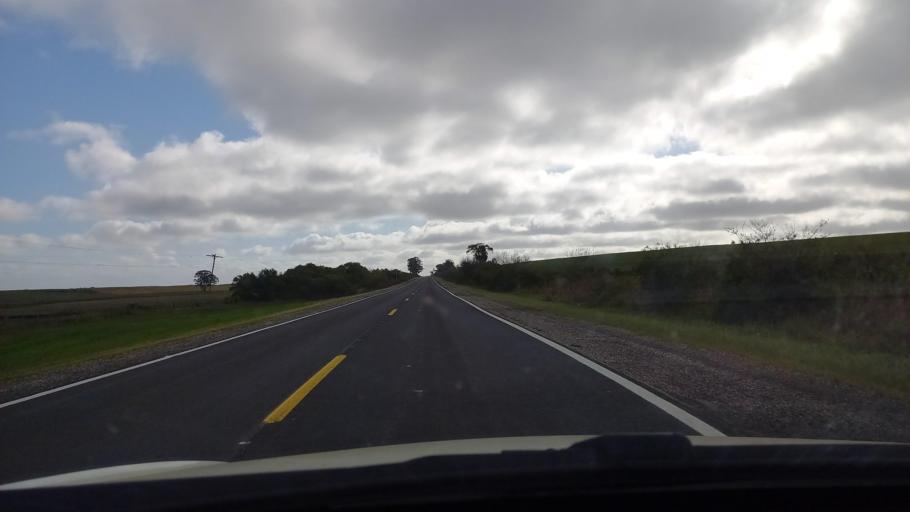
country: BR
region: Rio Grande do Sul
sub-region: Dom Pedrito
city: Dom Pedrito
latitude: -30.8956
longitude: -54.8478
